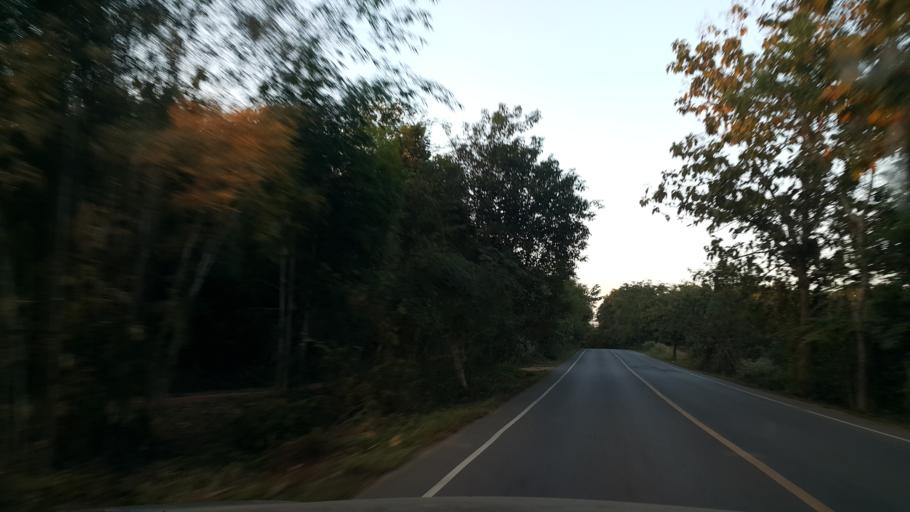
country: TH
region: Phrae
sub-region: Amphoe Wang Chin
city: Wang Chin
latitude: 17.8527
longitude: 99.6277
